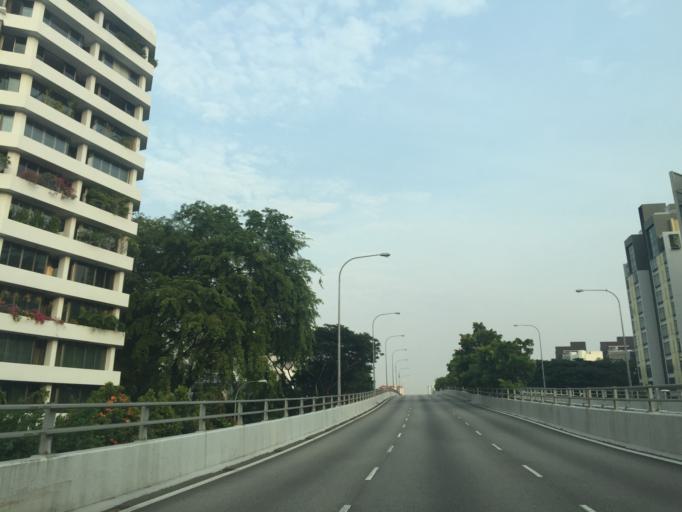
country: SG
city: Singapore
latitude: 1.3102
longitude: 103.8055
